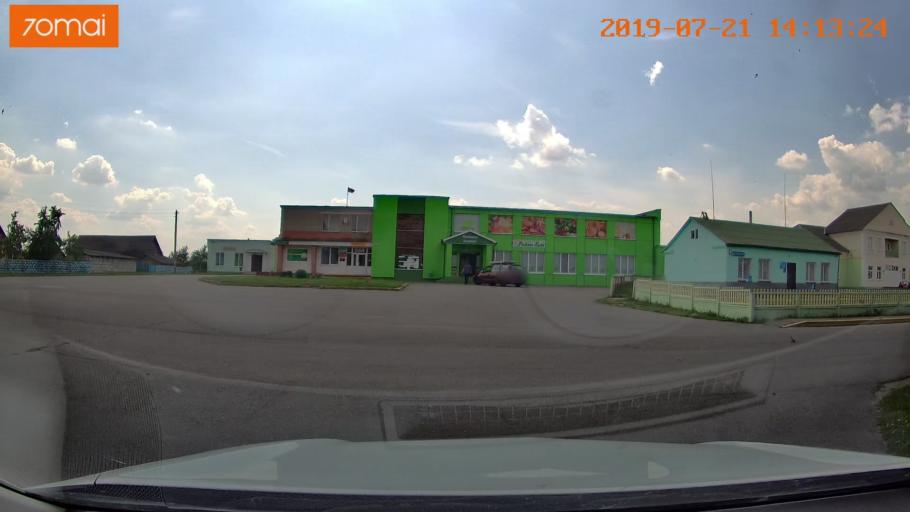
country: BY
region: Grodnenskaya
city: Karelichy
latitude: 53.6506
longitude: 26.1735
